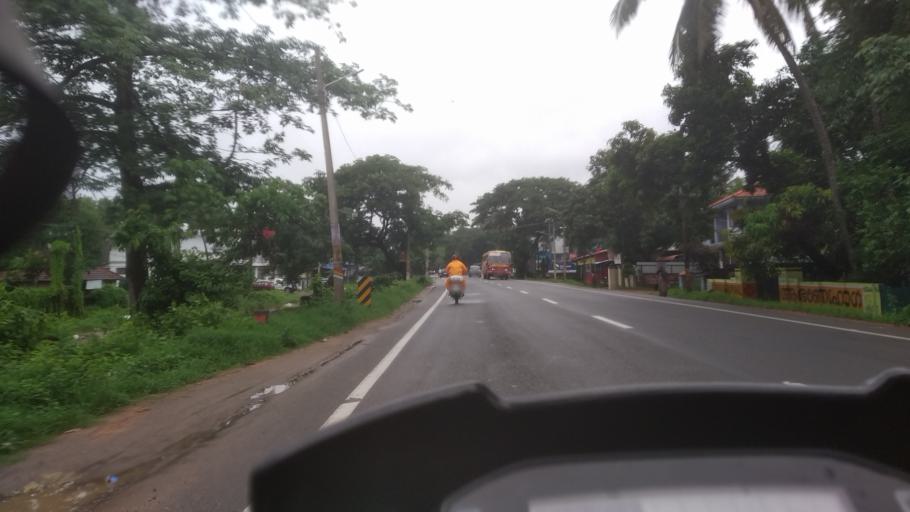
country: IN
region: Kerala
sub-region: Alappuzha
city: Kayankulam
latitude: 9.1826
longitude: 76.4910
